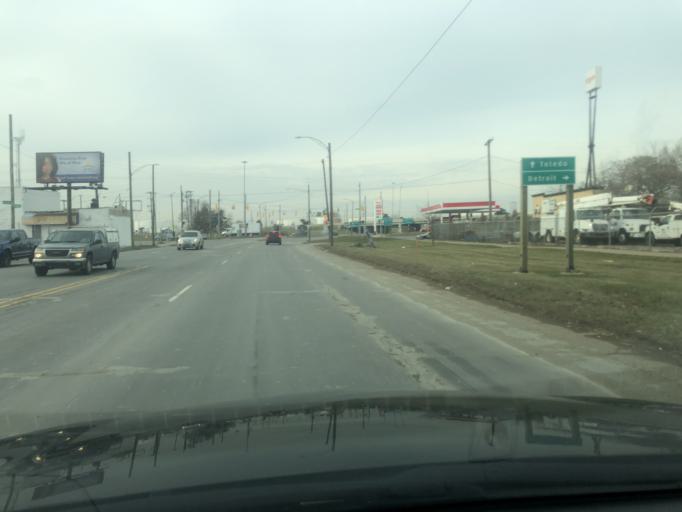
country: US
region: Michigan
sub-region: Wayne County
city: River Rouge
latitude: 42.2757
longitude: -83.1538
